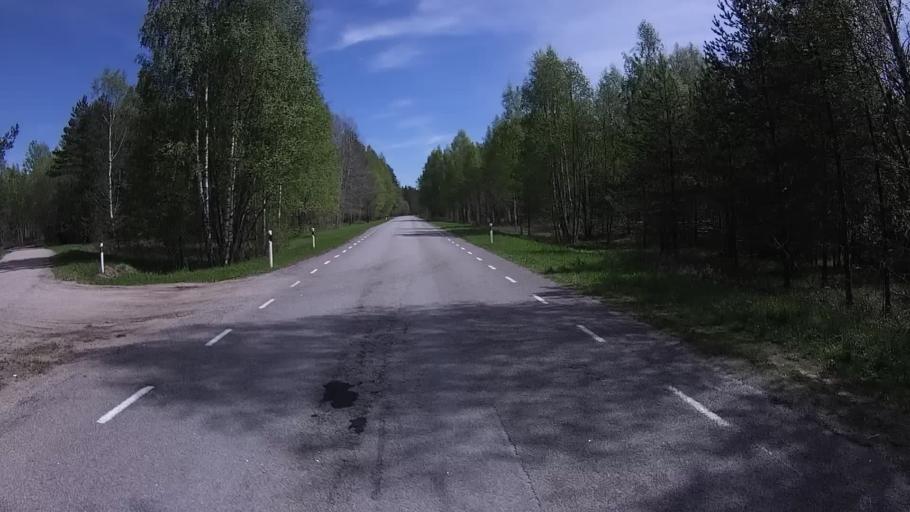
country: LV
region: Apes Novads
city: Ape
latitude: 57.6085
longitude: 26.4528
